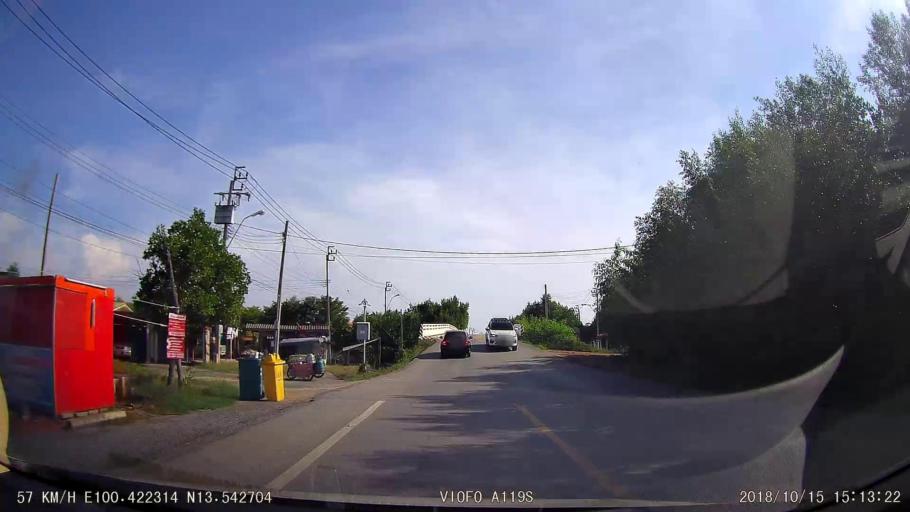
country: TH
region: Bangkok
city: Bang Khun Thian
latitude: 13.5424
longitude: 100.4224
